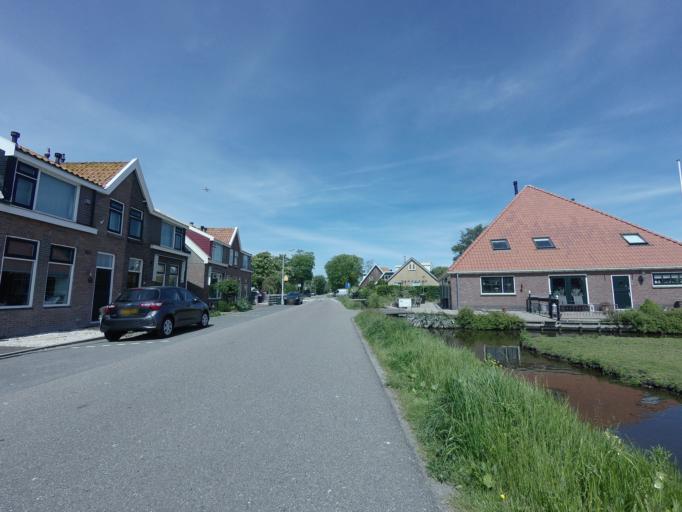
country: NL
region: North Holland
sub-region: Gemeente Velsen
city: Velsen-Zuid
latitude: 52.4477
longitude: 4.7222
